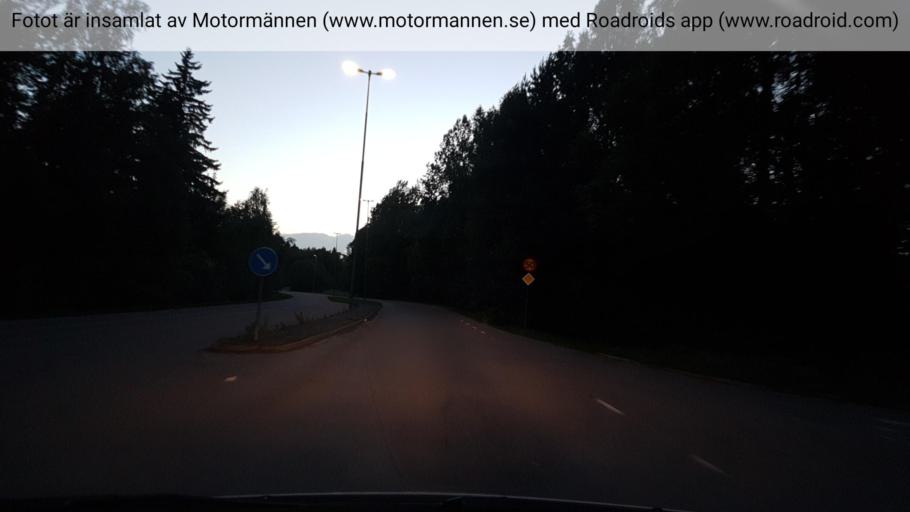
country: SE
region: Vaestmanland
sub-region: Vasteras
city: Vasteras
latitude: 59.6442
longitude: 16.5503
